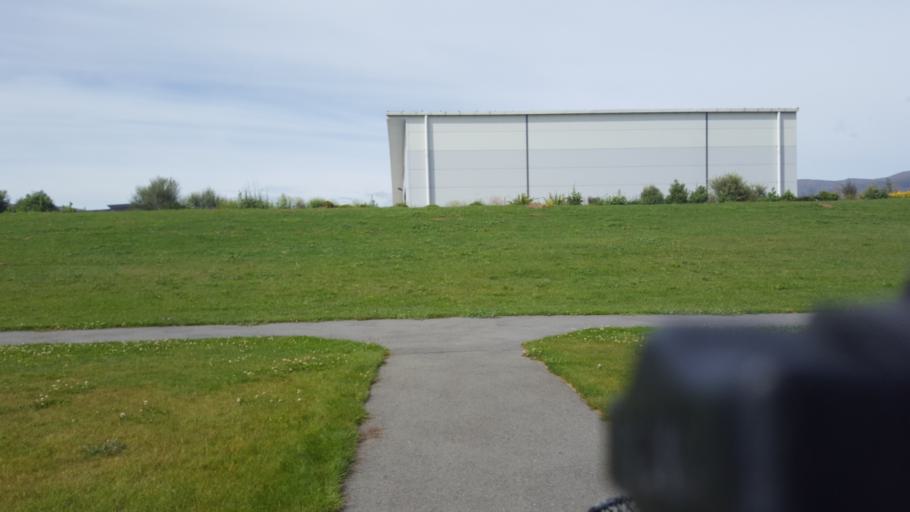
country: NZ
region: Otago
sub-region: Queenstown-Lakes District
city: Wanaka
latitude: -45.0485
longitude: 169.1879
